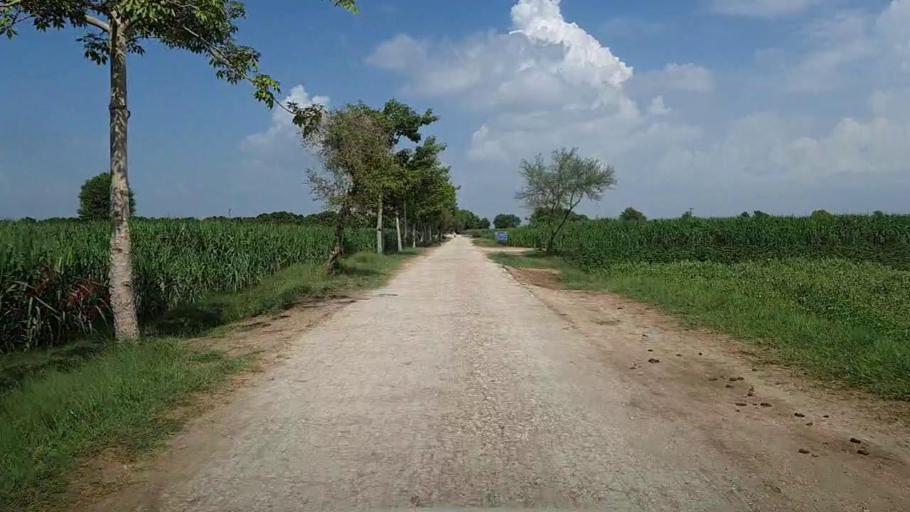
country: PK
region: Sindh
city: Bhiria
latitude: 26.9179
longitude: 68.2350
